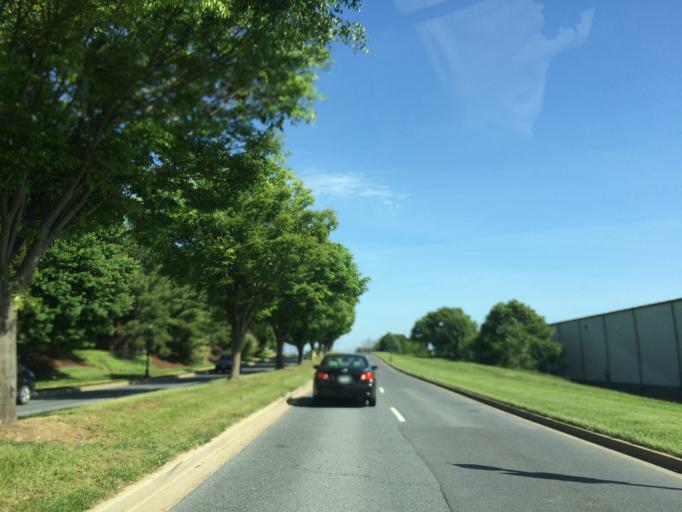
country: US
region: Maryland
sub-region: Frederick County
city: Clover Hill
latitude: 39.4508
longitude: -77.3890
